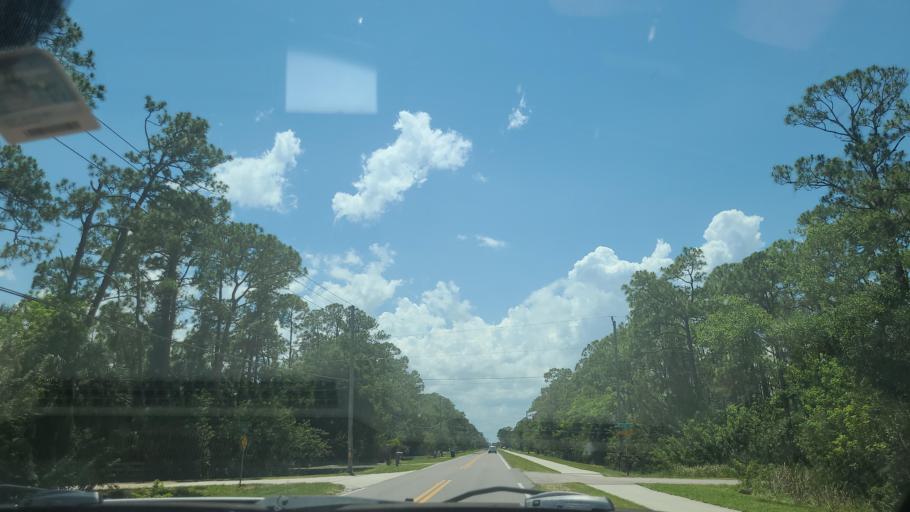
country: US
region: Florida
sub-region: Brevard County
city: Grant-Valkaria
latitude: 27.9537
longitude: -80.5793
